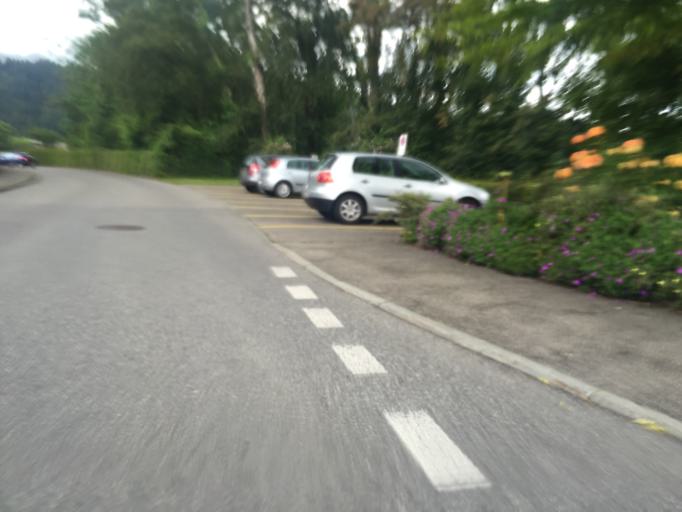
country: CH
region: Bern
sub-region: Bern-Mittelland District
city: Wohlen
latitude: 46.9665
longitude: 7.3724
